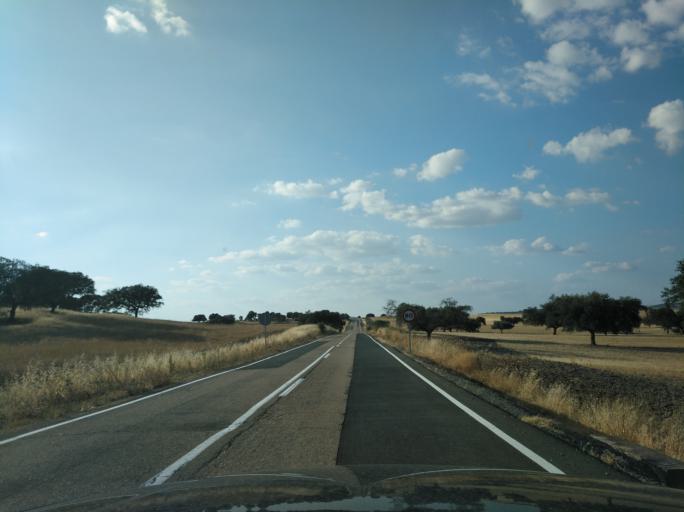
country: PT
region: Portalegre
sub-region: Campo Maior
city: Campo Maior
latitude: 39.1177
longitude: -7.0556
